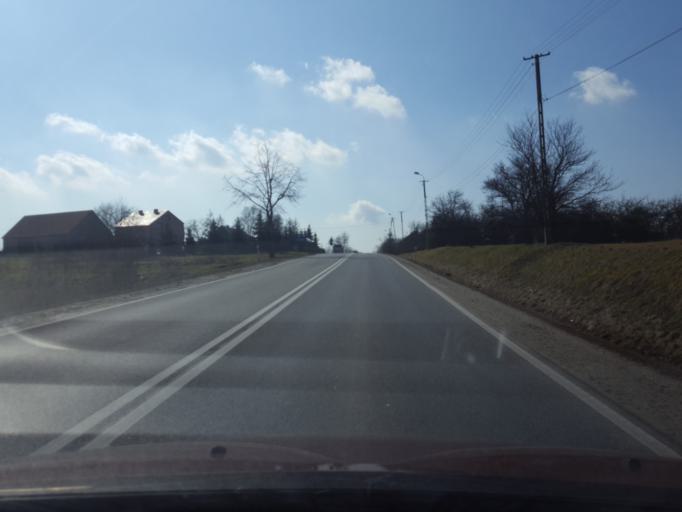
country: PL
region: Lesser Poland Voivodeship
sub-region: Powiat brzeski
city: Gnojnik
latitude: 49.8746
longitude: 20.6175
